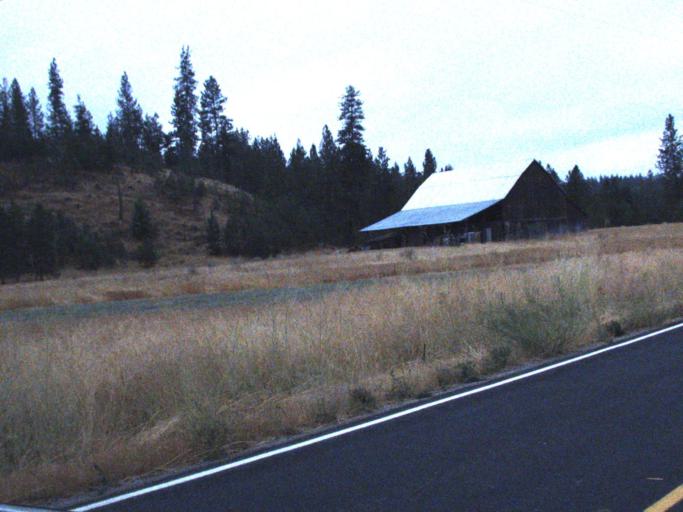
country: US
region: Washington
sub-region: Spokane County
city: Deer Park
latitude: 47.9136
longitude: -117.8006
